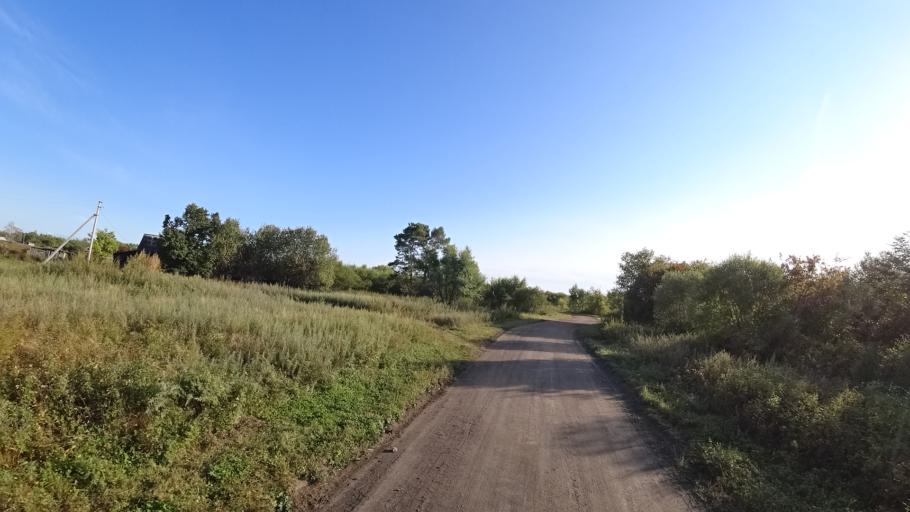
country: RU
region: Amur
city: Arkhara
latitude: 49.3561
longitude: 130.1160
